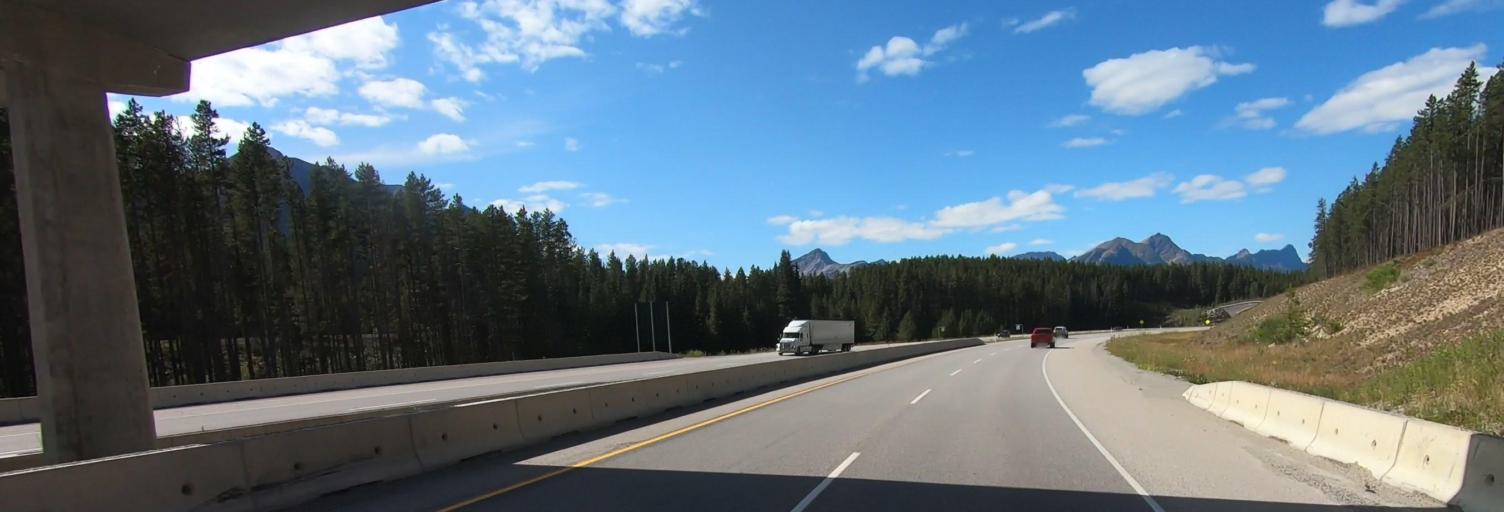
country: CA
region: Alberta
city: Lake Louise
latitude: 51.4332
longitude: -116.1898
